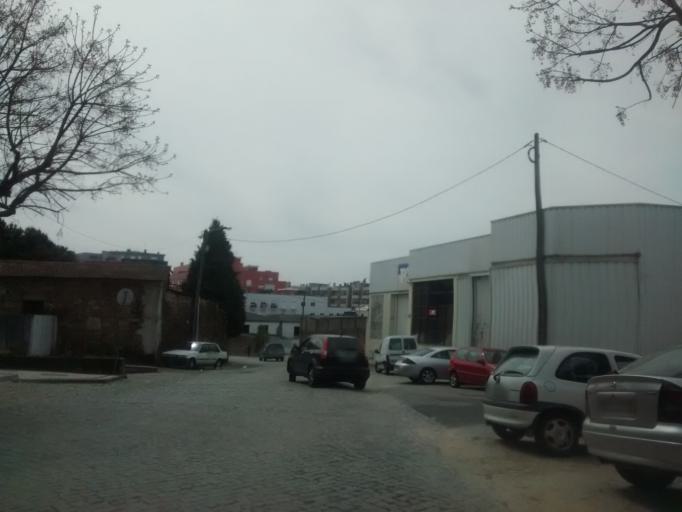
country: PT
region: Braga
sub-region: Braga
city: Braga
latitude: 41.5566
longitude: -8.4039
